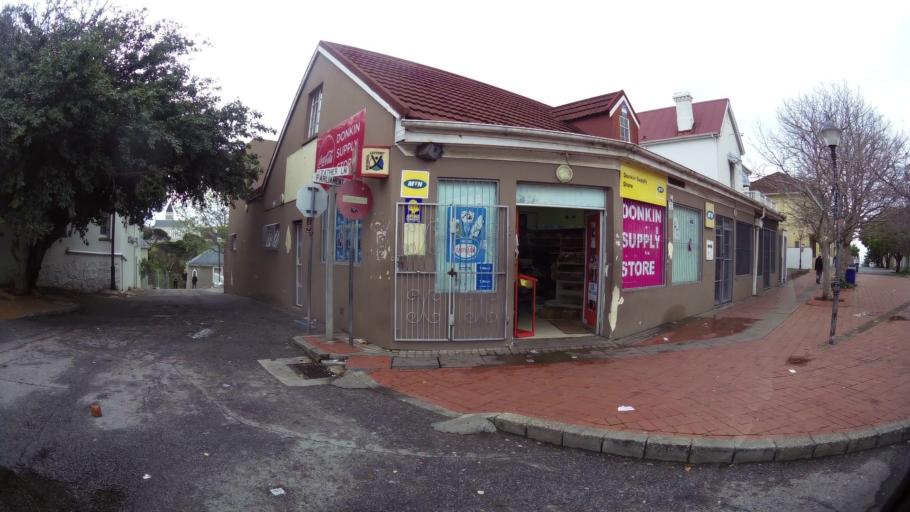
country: ZA
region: Eastern Cape
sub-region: Nelson Mandela Bay Metropolitan Municipality
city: Port Elizabeth
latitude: -33.9617
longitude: 25.6162
